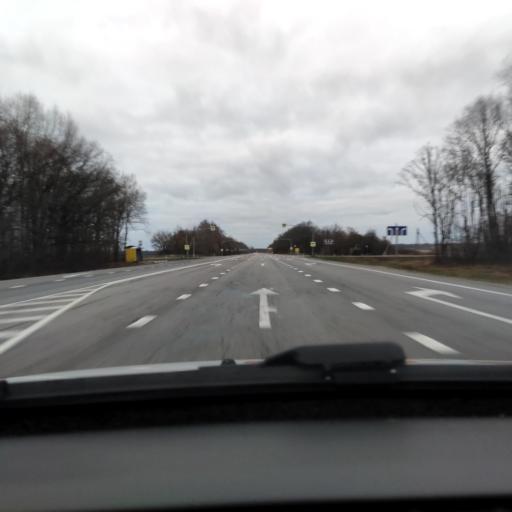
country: RU
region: Lipetsk
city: Khlevnoye
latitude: 52.3076
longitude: 39.1668
